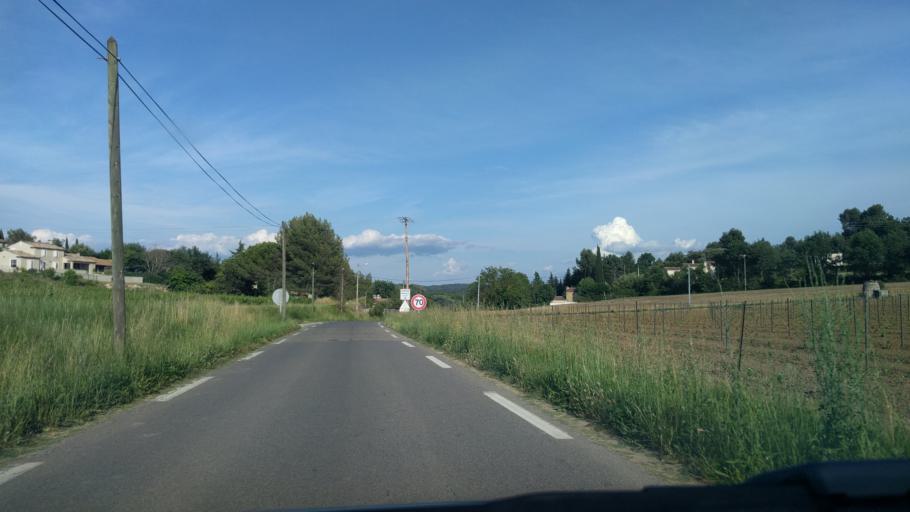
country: FR
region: Provence-Alpes-Cote d'Azur
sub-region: Departement du Vaucluse
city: Pertuis
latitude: 43.7333
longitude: 5.5336
